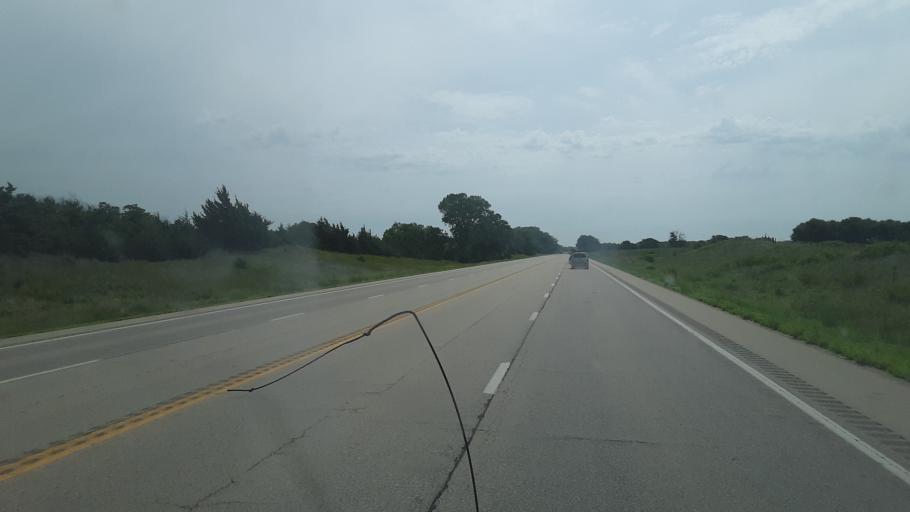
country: US
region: Kansas
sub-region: Rice County
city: Sterling
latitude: 37.9847
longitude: -98.2867
